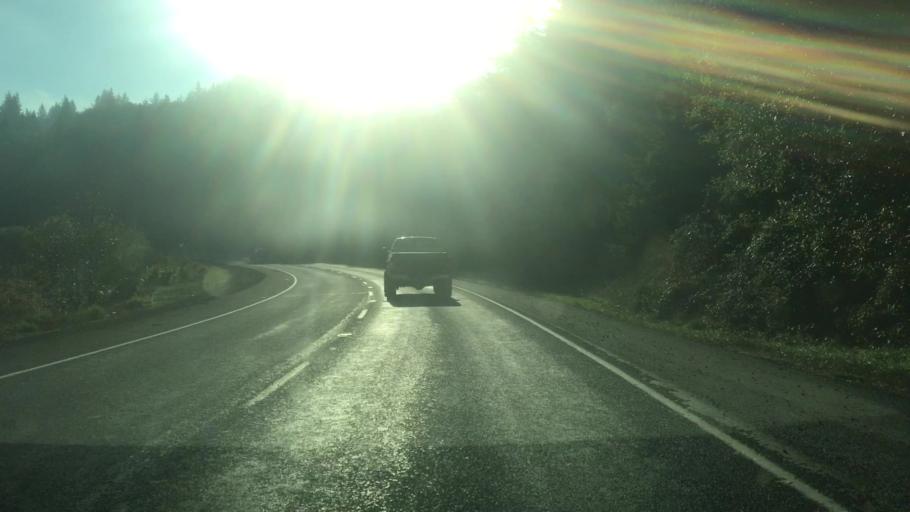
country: US
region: Oregon
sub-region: Clatsop County
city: Astoria
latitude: 46.2603
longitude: -123.8513
